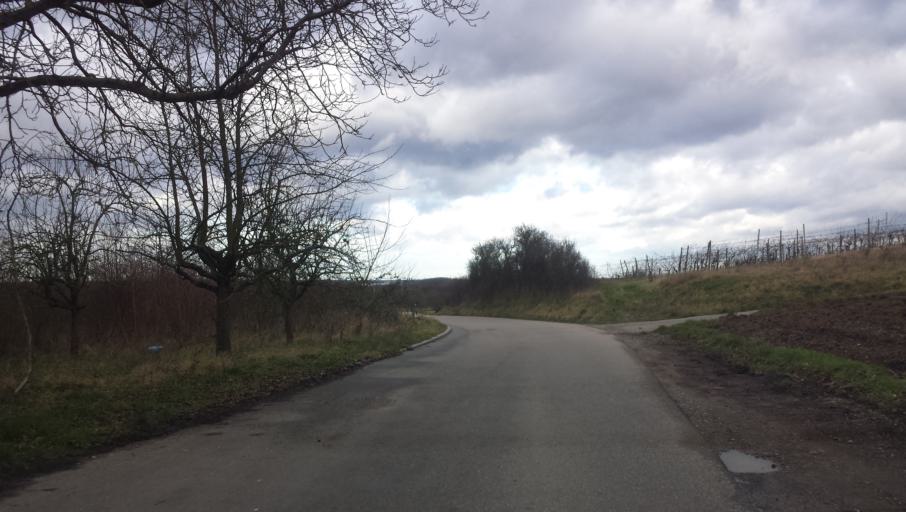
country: DE
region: Baden-Wuerttemberg
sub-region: Karlsruhe Region
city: Malsch
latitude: 49.2592
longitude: 8.6828
